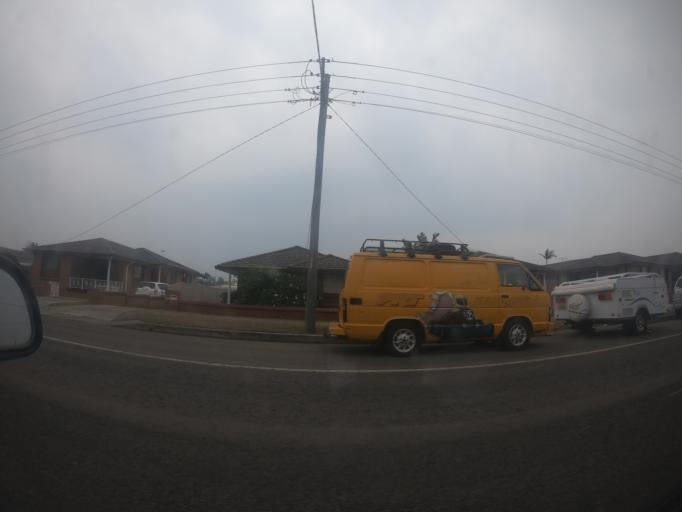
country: AU
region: New South Wales
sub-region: Shellharbour
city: Lake Illawarra
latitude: -34.5519
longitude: 150.8673
